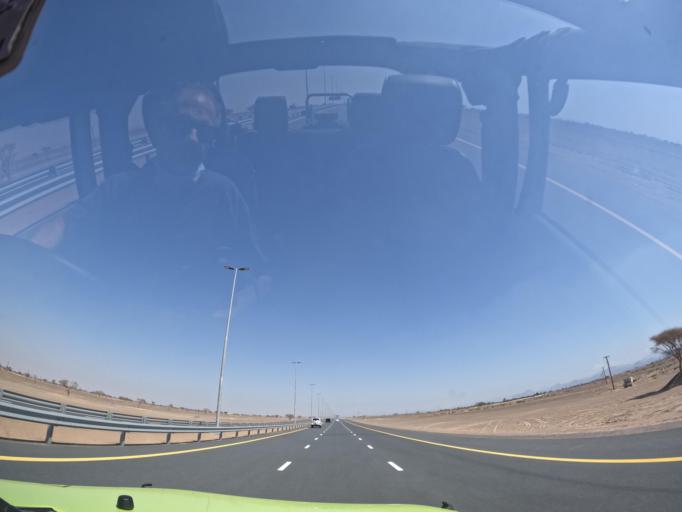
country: AE
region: Ash Shariqah
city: Adh Dhayd
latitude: 25.0867
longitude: 55.9189
